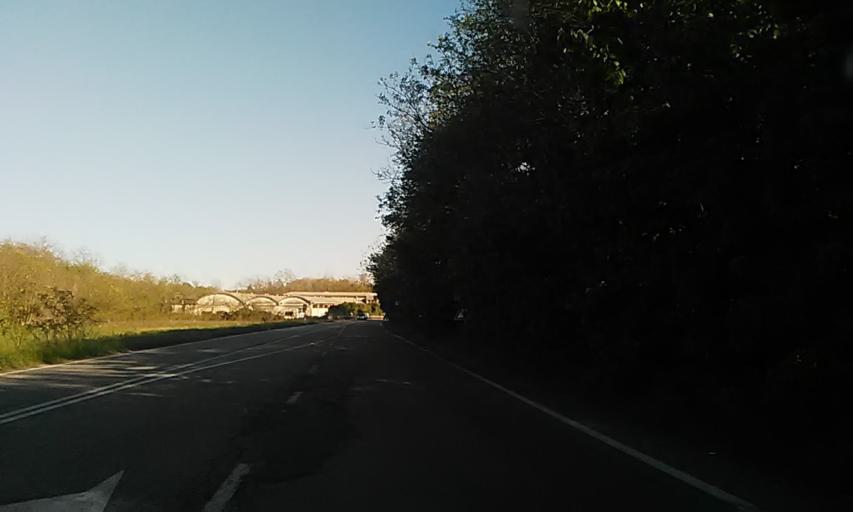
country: IT
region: Piedmont
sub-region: Provincia di Novara
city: Vaprio D'Agogna
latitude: 45.5980
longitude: 8.5354
